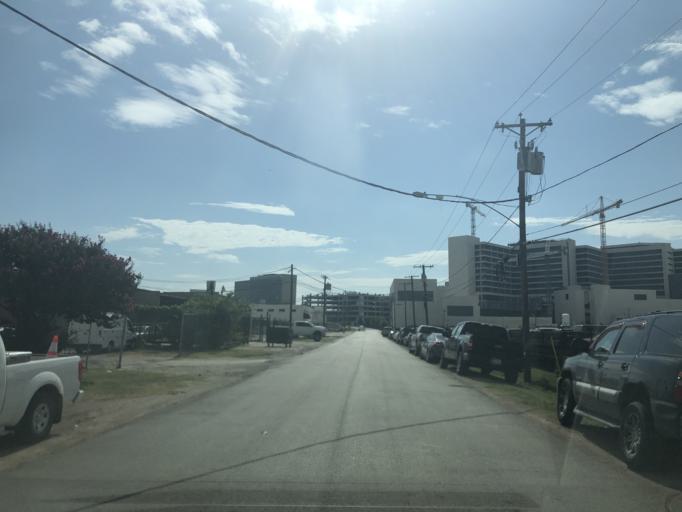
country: US
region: Texas
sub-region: Dallas County
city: Dallas
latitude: 32.8213
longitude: -96.8541
